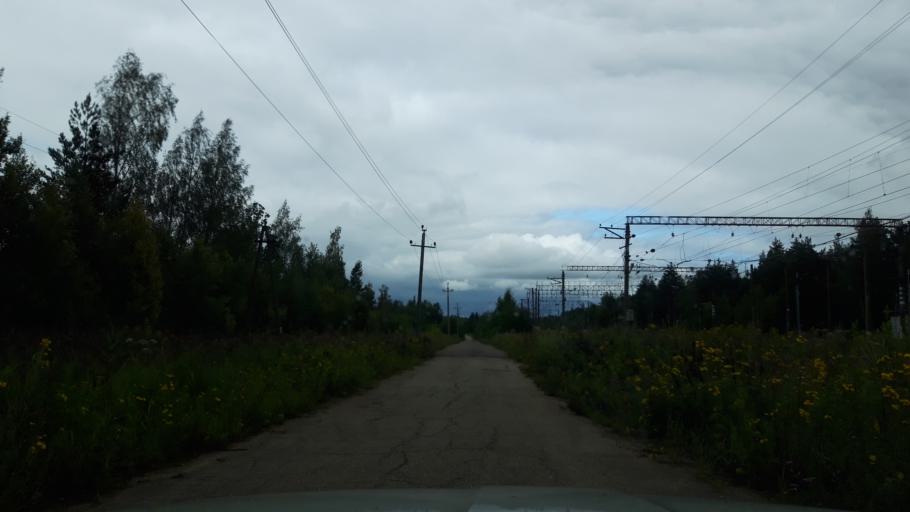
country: RU
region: Moskovskaya
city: Povarovo
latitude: 56.0393
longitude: 37.0537
